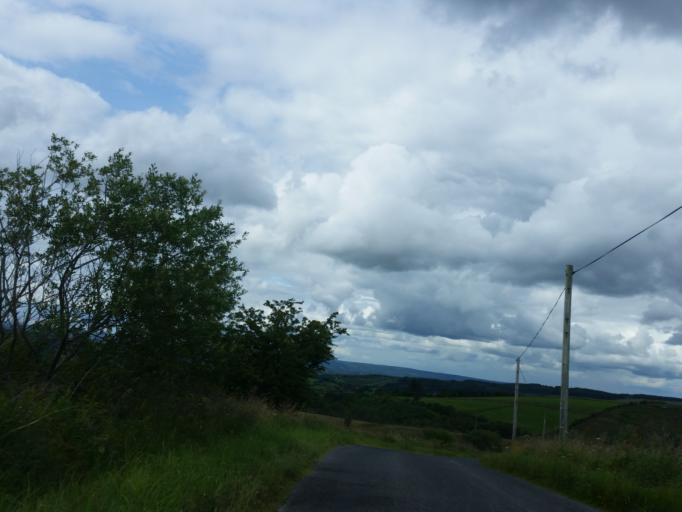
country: IE
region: Ulster
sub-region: County Monaghan
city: Clones
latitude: 54.2717
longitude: -7.2743
